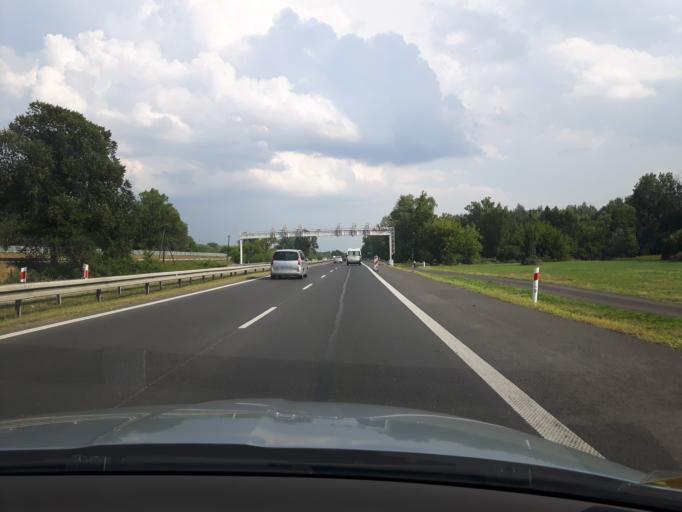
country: PL
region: Masovian Voivodeship
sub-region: Powiat nowodworski
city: Nowy Dwor Mazowiecki
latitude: 52.4068
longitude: 20.7028
